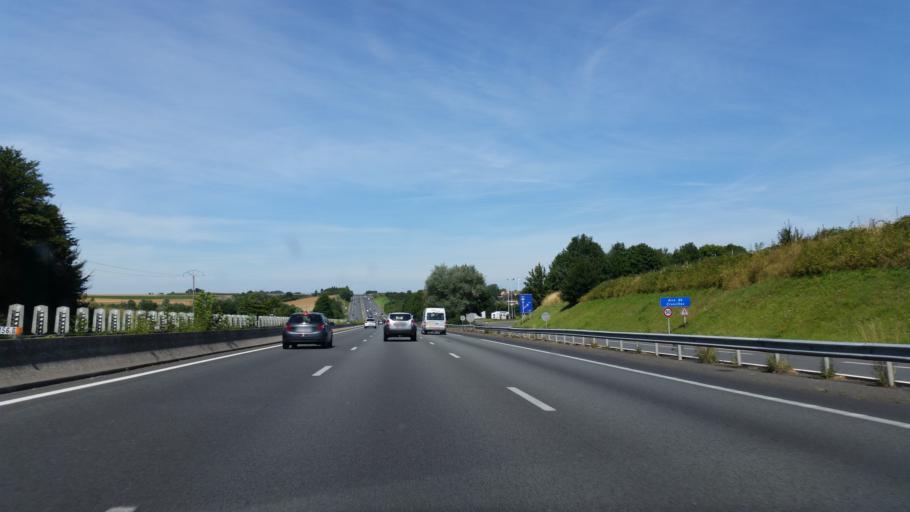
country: FR
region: Nord-Pas-de-Calais
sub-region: Departement du Pas-de-Calais
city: Croisilles
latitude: 50.1883
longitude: 2.8730
